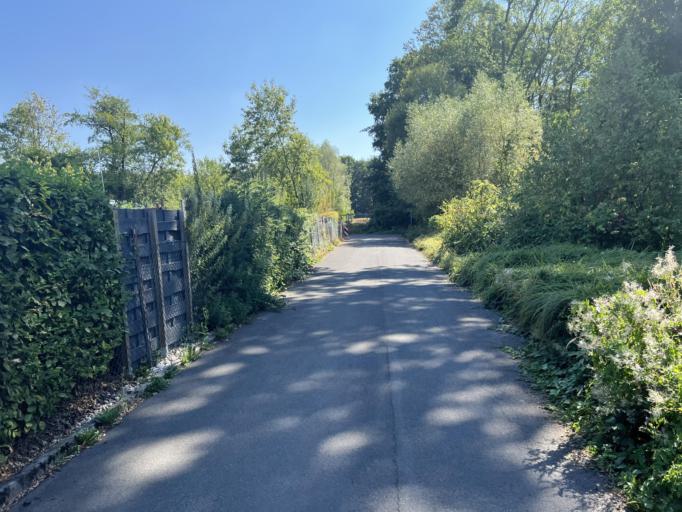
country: DE
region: Hesse
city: Heusenstamm
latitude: 50.0775
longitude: 8.8148
